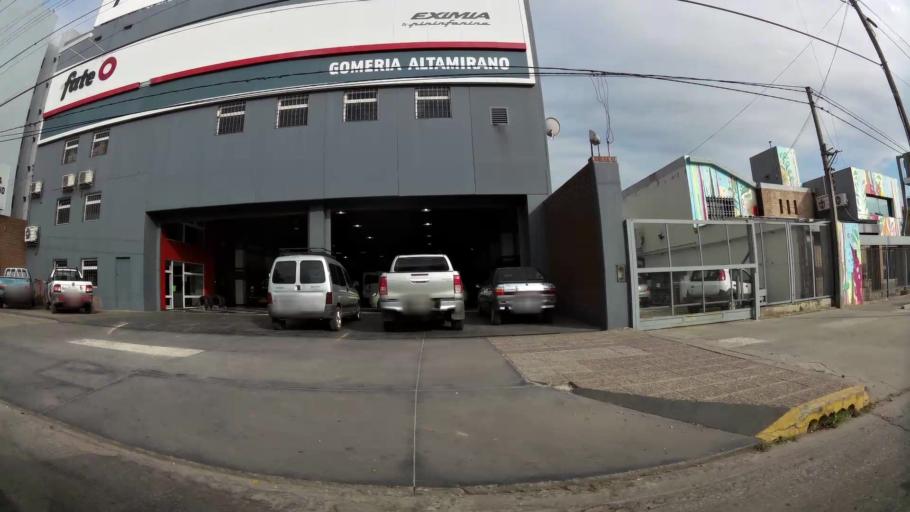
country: AR
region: Cordoba
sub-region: Departamento de Capital
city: Cordoba
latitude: -31.4343
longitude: -64.1948
